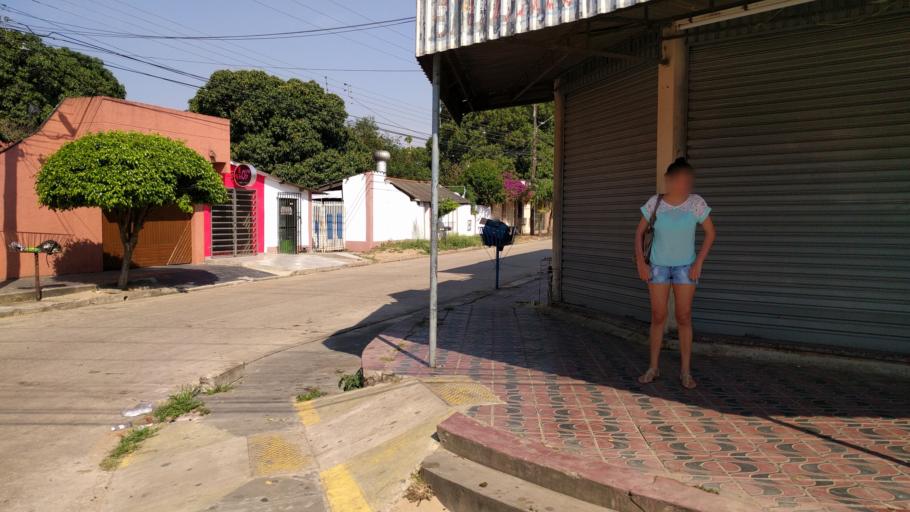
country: BO
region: Santa Cruz
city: Santa Cruz de la Sierra
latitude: -17.8129
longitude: -63.1789
